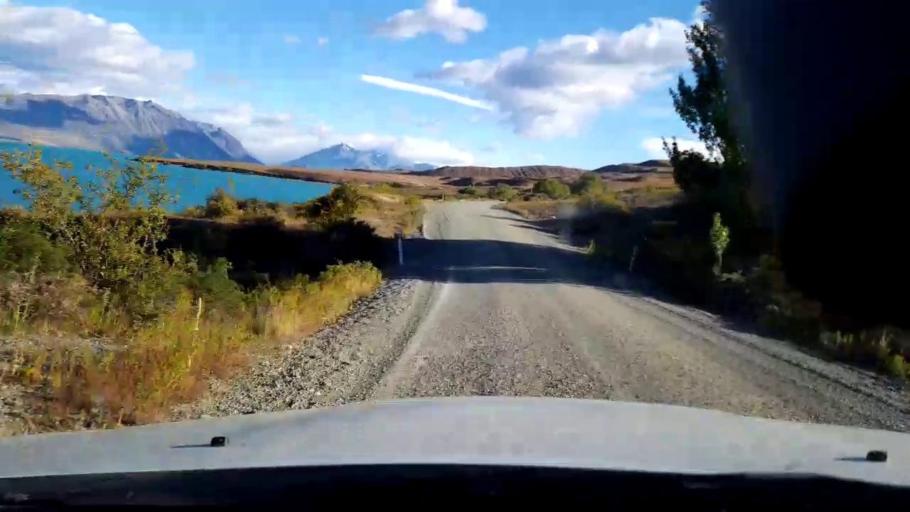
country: NZ
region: Canterbury
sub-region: Timaru District
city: Pleasant Point
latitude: -43.9330
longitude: 170.5589
